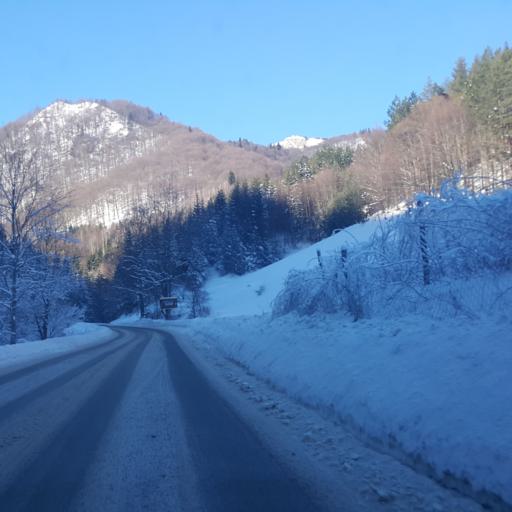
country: XK
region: Mitrovica
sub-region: Komuna e Leposaviqit
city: Leposaviq
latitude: 43.3061
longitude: 20.8648
